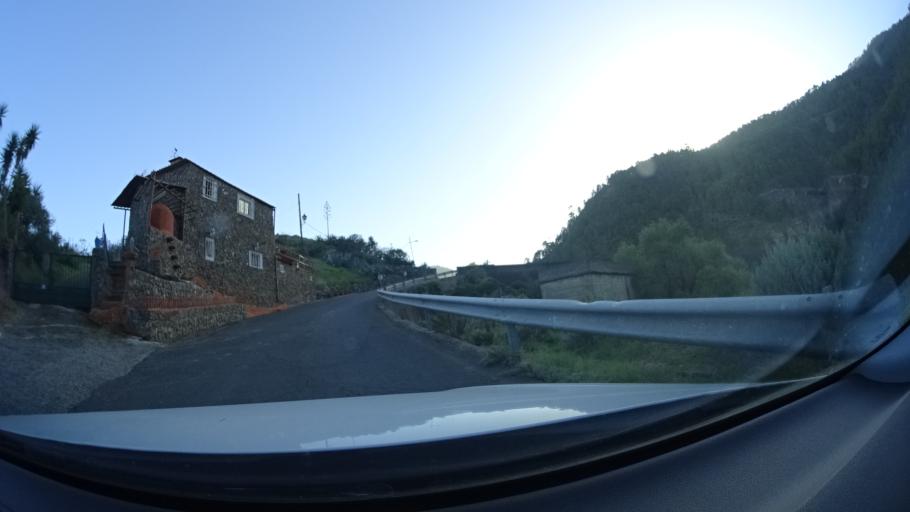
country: ES
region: Canary Islands
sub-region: Provincia de Las Palmas
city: Artenara
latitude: 28.0472
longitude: -15.6722
